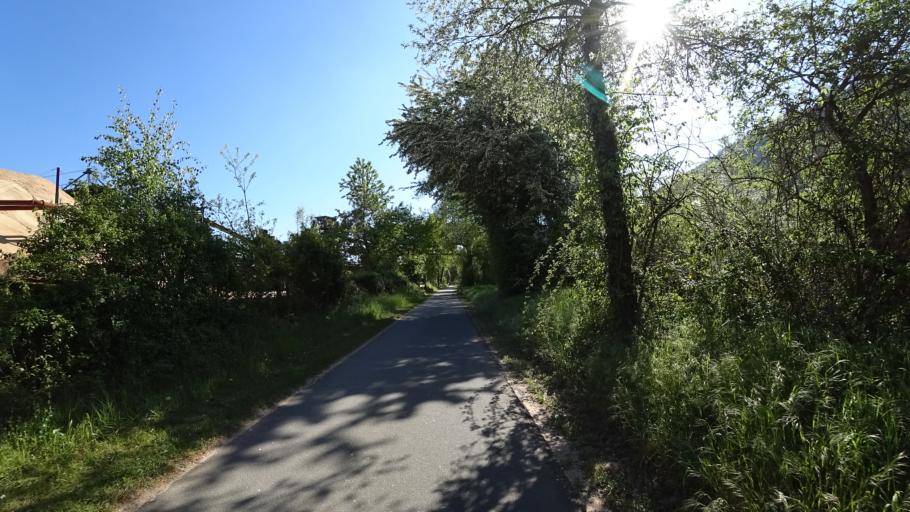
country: DE
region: Bavaria
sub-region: Regierungsbezirk Unterfranken
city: Burgstadt
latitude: 49.7373
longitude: 9.2765
